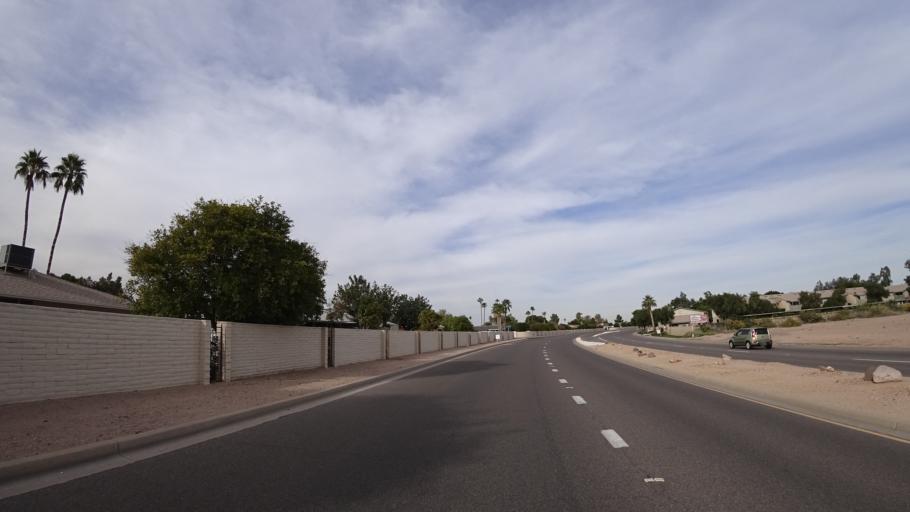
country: US
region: Arizona
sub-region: Maricopa County
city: Sun City
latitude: 33.5679
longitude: -112.2762
